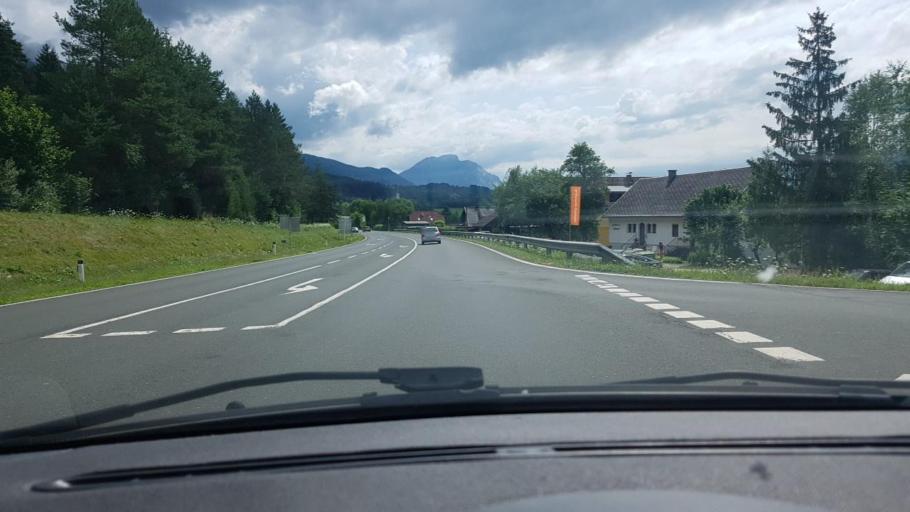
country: AT
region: Carinthia
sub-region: Politischer Bezirk Hermagor
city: Hermagor
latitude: 46.6306
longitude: 13.4532
